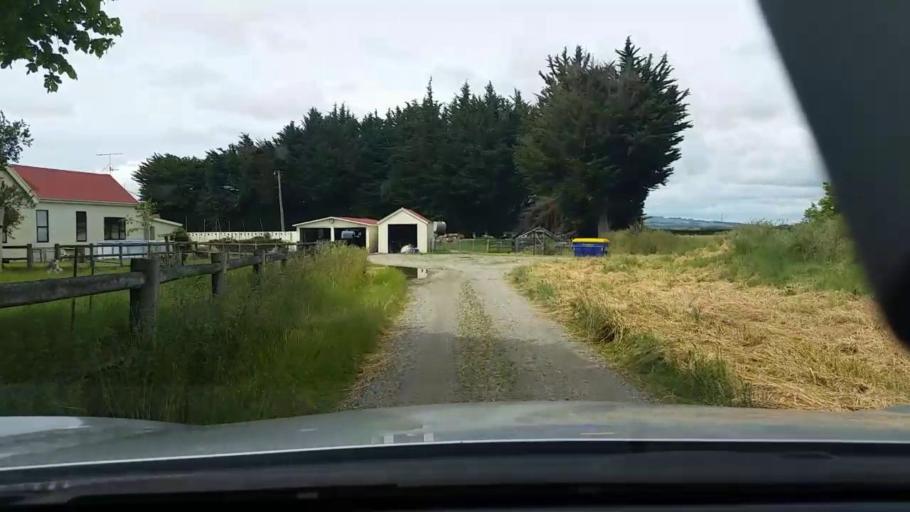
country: NZ
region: Southland
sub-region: Gore District
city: Gore
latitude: -46.1247
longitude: 168.9316
